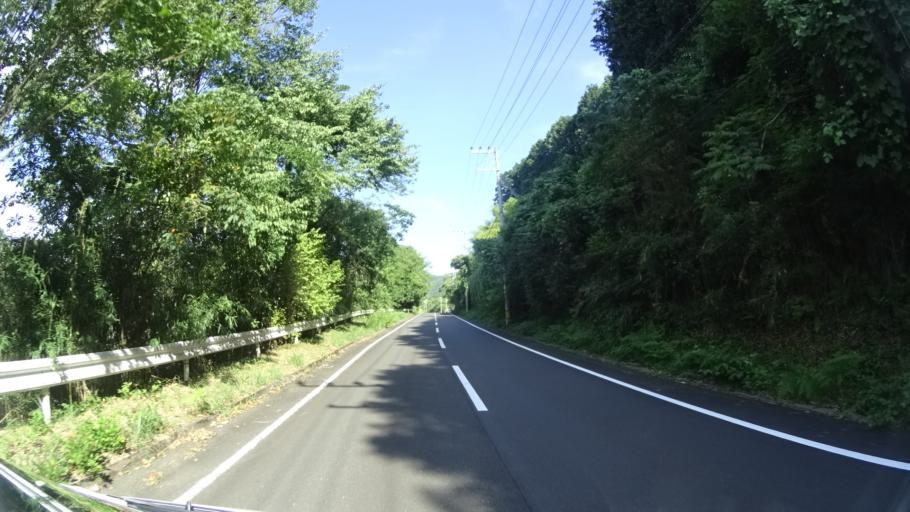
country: JP
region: Kyoto
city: Ayabe
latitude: 35.2865
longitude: 135.2862
